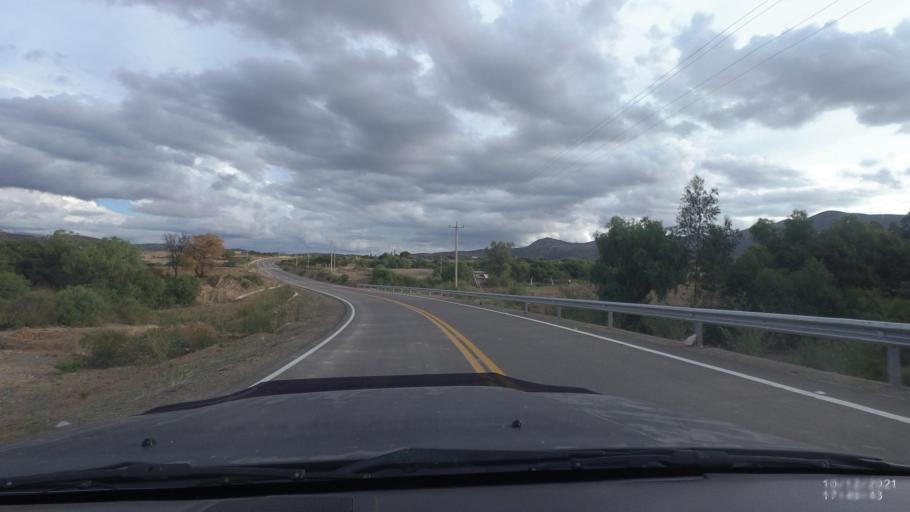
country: BO
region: Cochabamba
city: Tarata
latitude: -17.6589
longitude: -65.9681
